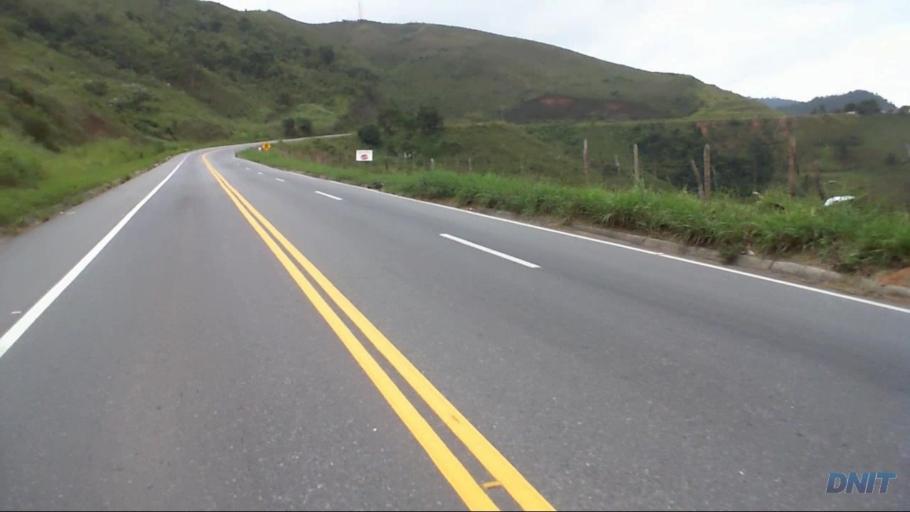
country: BR
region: Minas Gerais
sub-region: Nova Era
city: Nova Era
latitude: -19.6874
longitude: -42.9896
